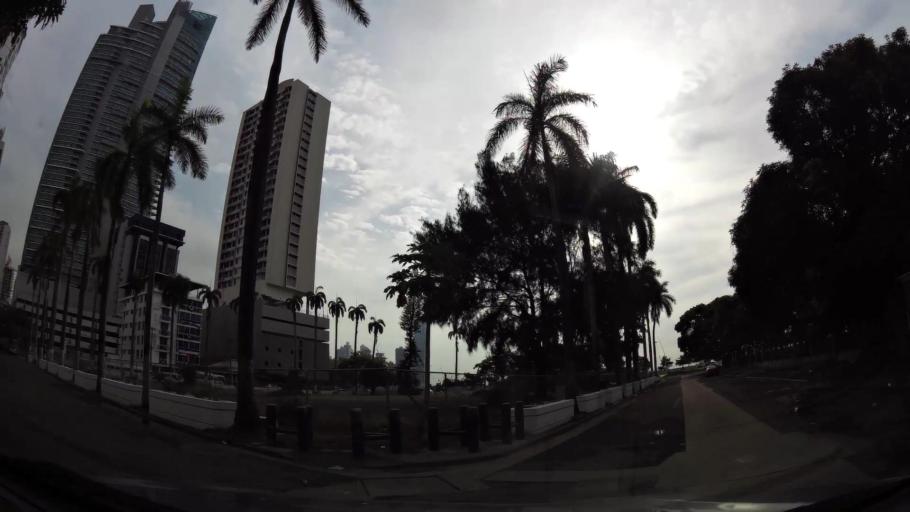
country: PA
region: Panama
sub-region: Distrito de Panama
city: Ancon
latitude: 8.9703
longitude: -79.5315
